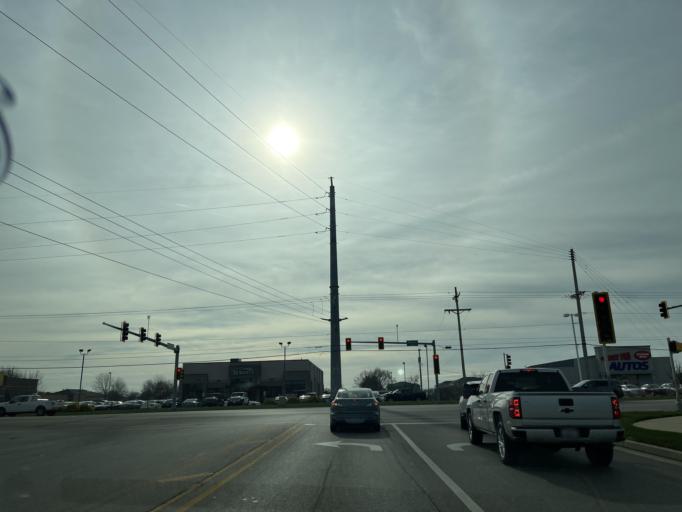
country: US
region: Illinois
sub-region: Sangamon County
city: Jerome
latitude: 39.7568
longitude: -89.7344
